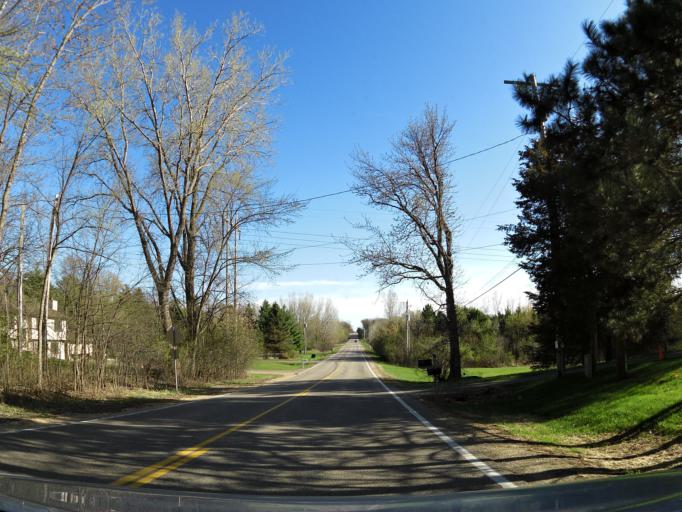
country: US
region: Minnesota
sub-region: Washington County
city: Lake Elmo
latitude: 44.9573
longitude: -92.8427
